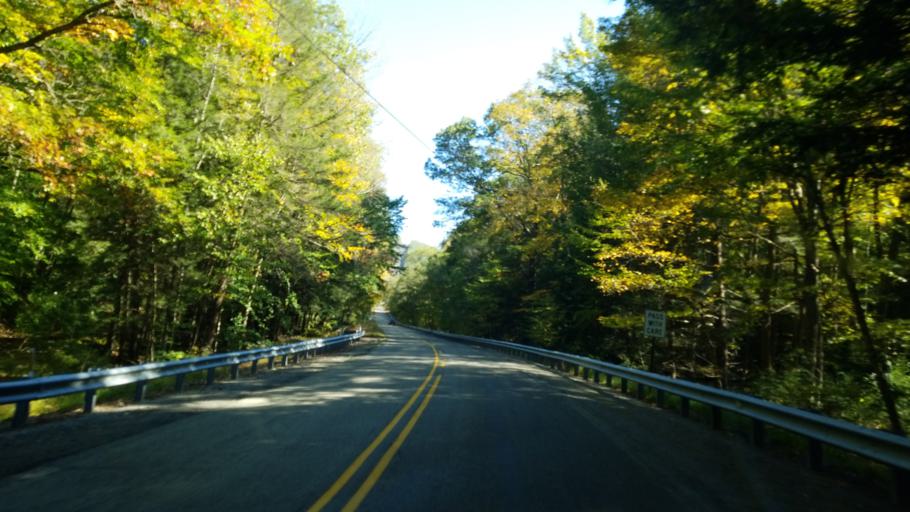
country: US
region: Pennsylvania
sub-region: Elk County
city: Saint Marys
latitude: 41.2668
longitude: -78.4023
